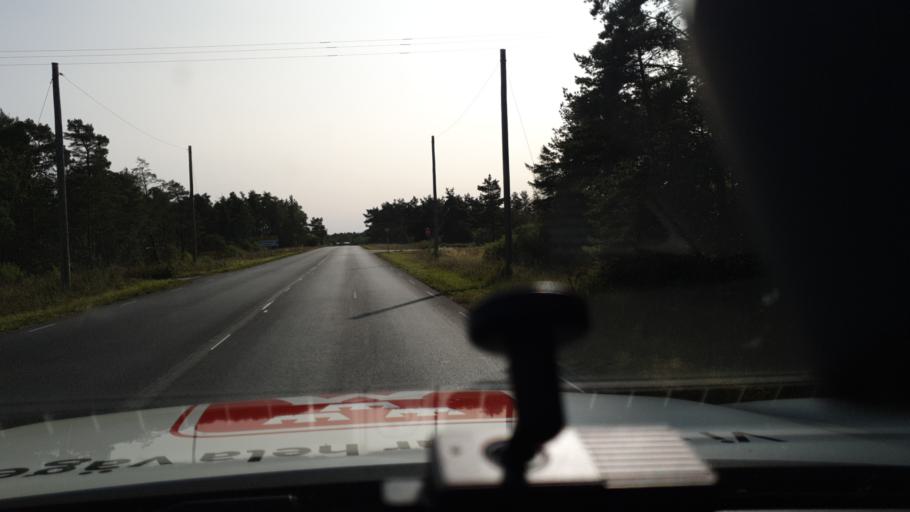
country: SE
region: Gotland
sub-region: Gotland
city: Slite
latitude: 57.7284
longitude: 18.7896
